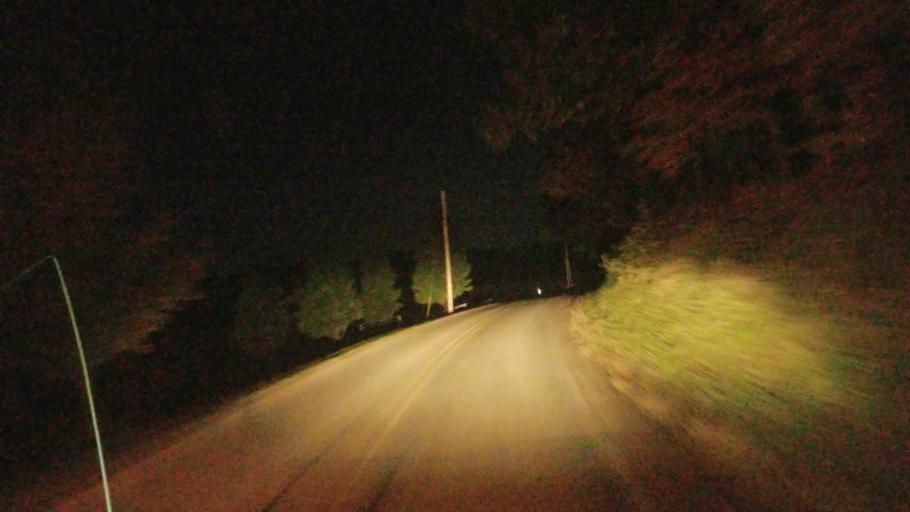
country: US
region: Ohio
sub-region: Perry County
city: Somerset
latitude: 39.8769
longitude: -82.2025
